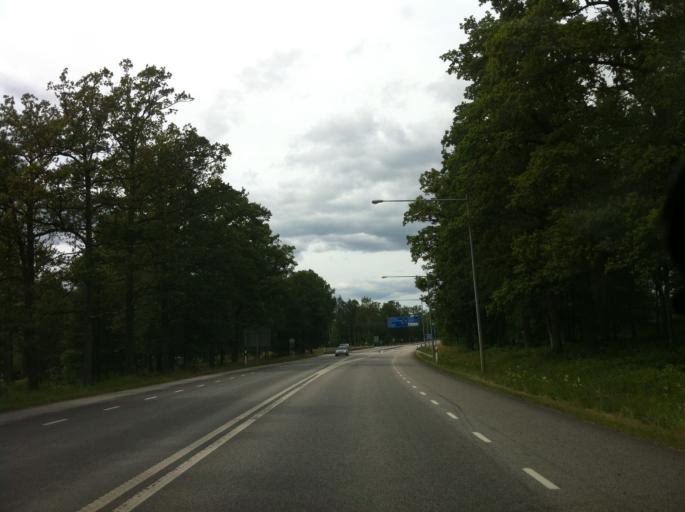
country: SE
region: Kronoberg
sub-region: Tingsryds Kommun
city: Tingsryd
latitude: 56.5277
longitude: 14.9665
